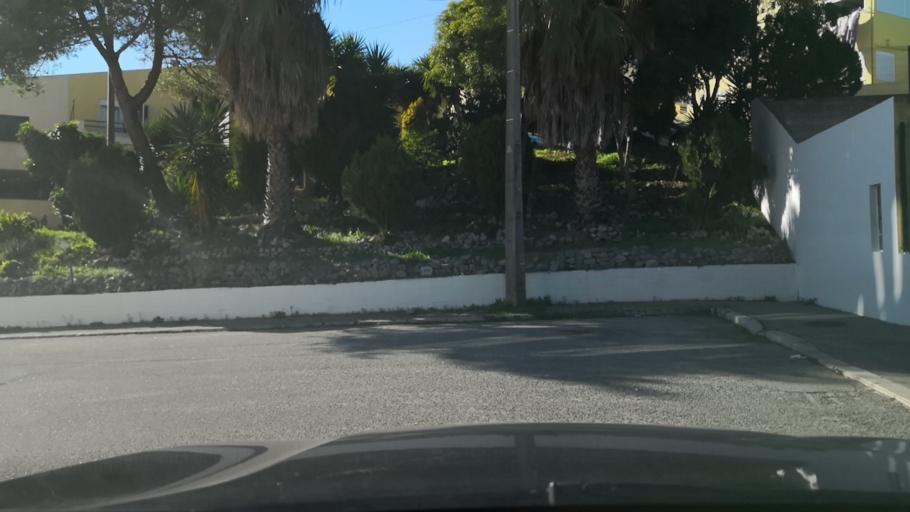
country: PT
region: Setubal
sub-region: Setubal
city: Setubal
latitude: 38.5280
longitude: -8.9090
